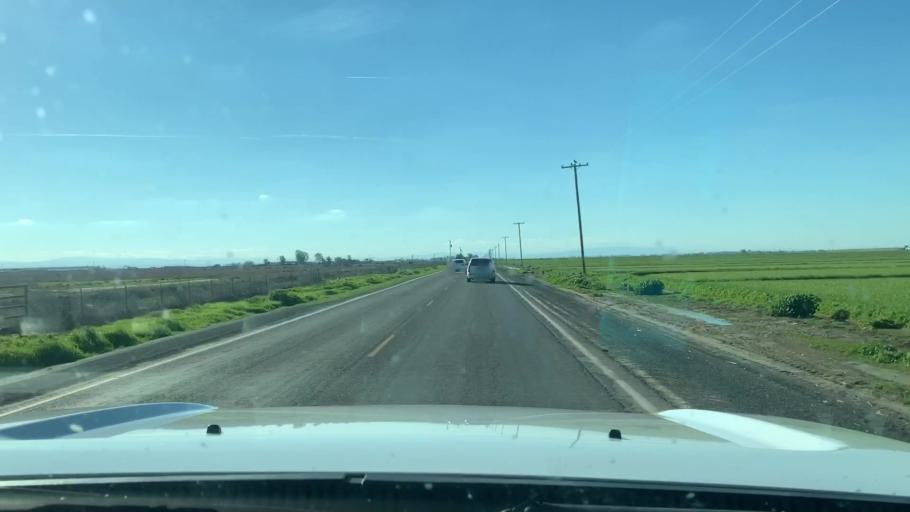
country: US
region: California
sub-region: Kings County
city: Home Garden
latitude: 36.2112
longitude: -119.6630
